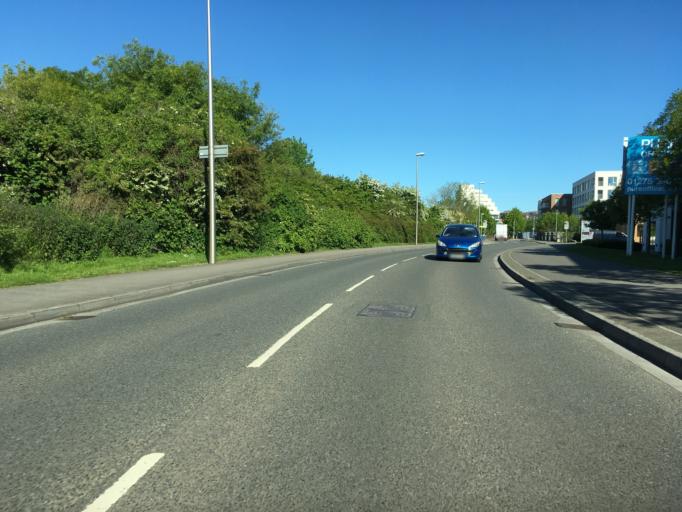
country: GB
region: England
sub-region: North Somerset
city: Portishead
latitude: 51.4846
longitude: -2.7600
